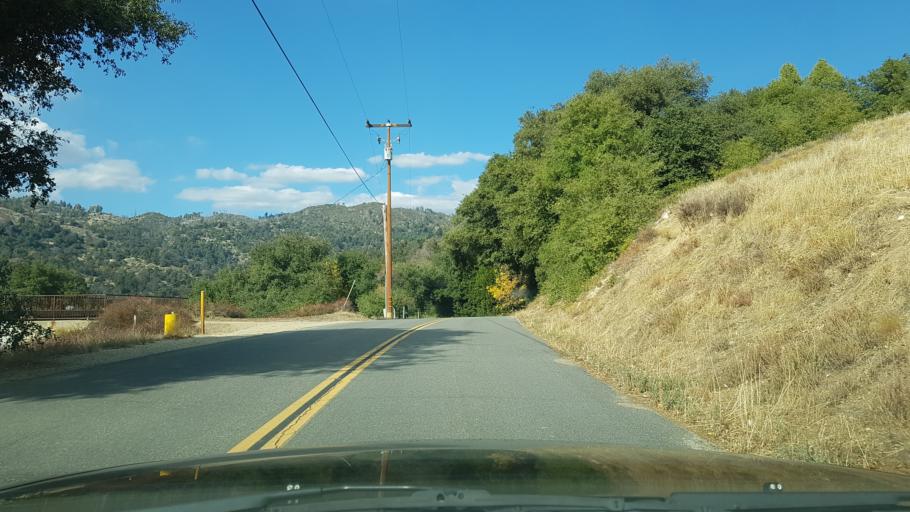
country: US
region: California
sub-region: San Diego County
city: Julian
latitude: 33.1154
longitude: -116.6030
